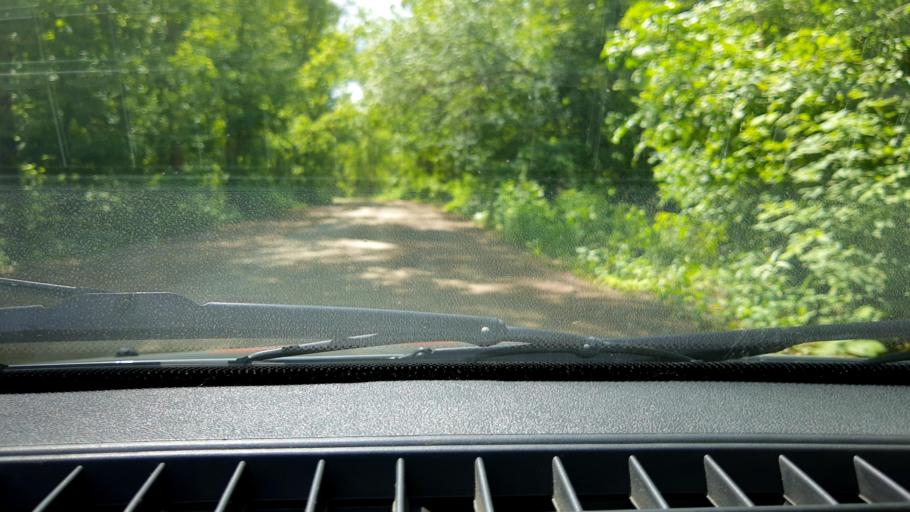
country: RU
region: Bashkortostan
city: Ufa
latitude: 54.6793
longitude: 56.0609
